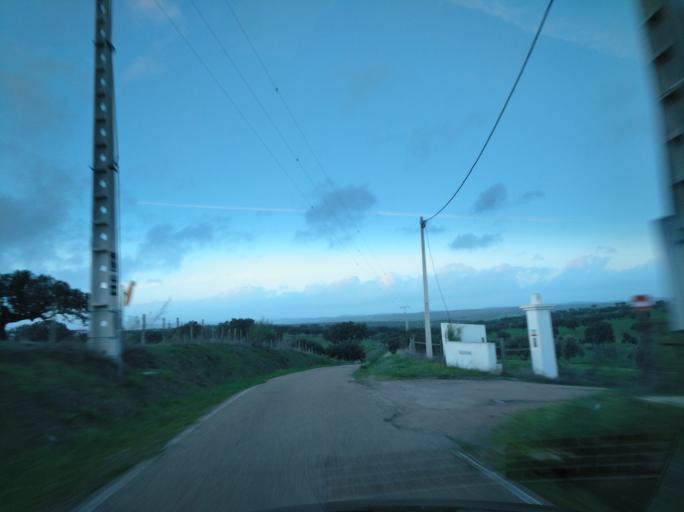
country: PT
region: Portalegre
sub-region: Campo Maior
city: Campo Maior
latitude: 39.0755
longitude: -7.1159
